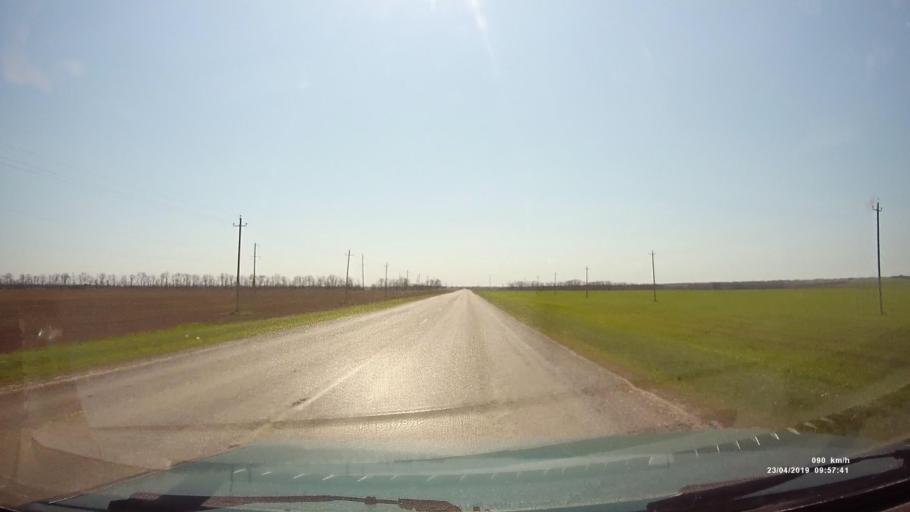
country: RU
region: Rostov
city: Sovetskoye
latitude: 46.7866
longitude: 42.0889
